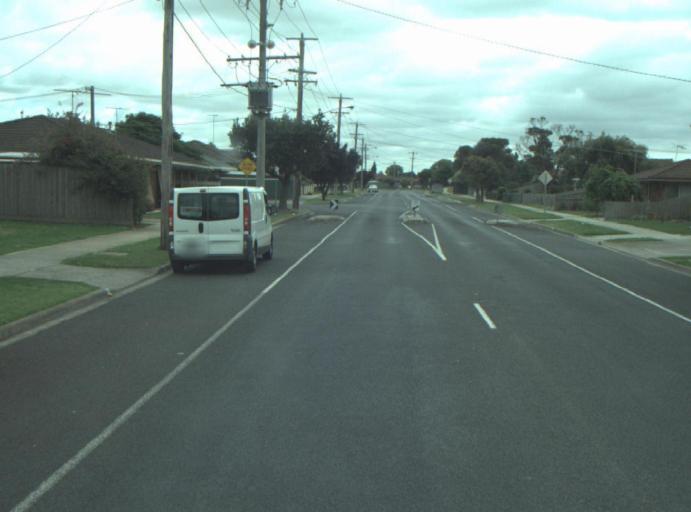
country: AU
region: Victoria
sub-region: Greater Geelong
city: Bell Post Hill
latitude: -38.0716
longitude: 144.3440
